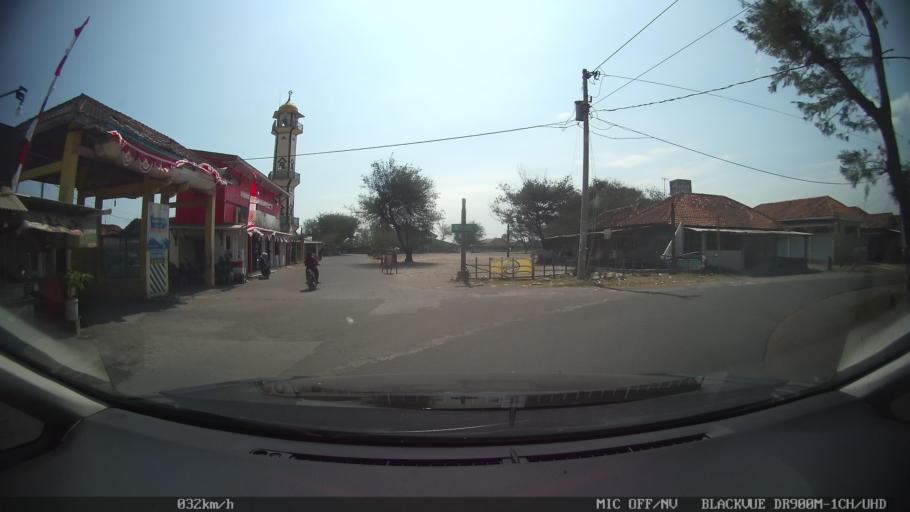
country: ID
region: Daerah Istimewa Yogyakarta
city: Bambanglipuro
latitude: -8.0129
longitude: 110.2937
